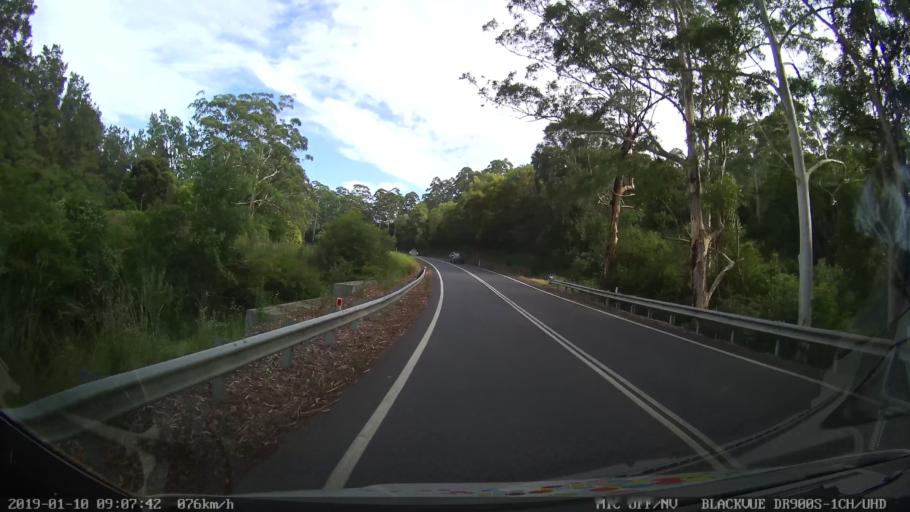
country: AU
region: New South Wales
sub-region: Coffs Harbour
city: Nana Glen
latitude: -30.2366
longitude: 153.0272
